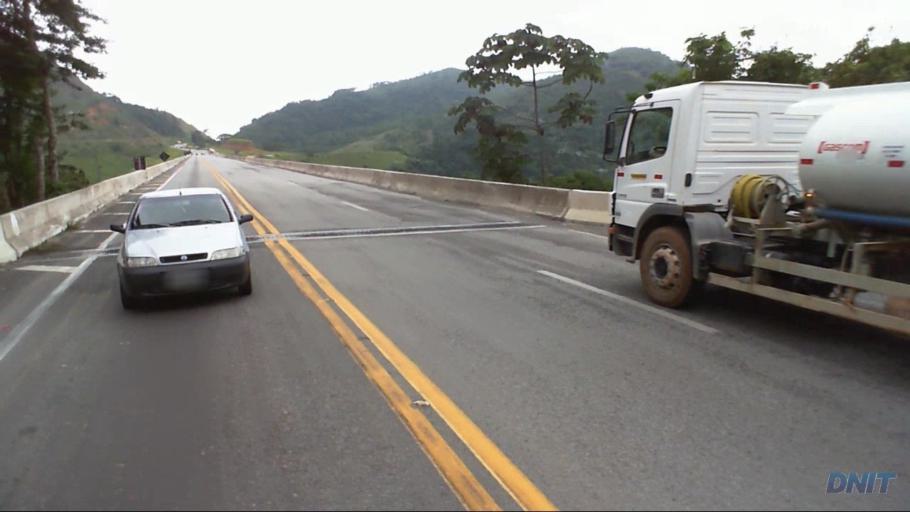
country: BR
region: Minas Gerais
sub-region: Nova Era
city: Nova Era
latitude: -19.6560
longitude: -42.9580
